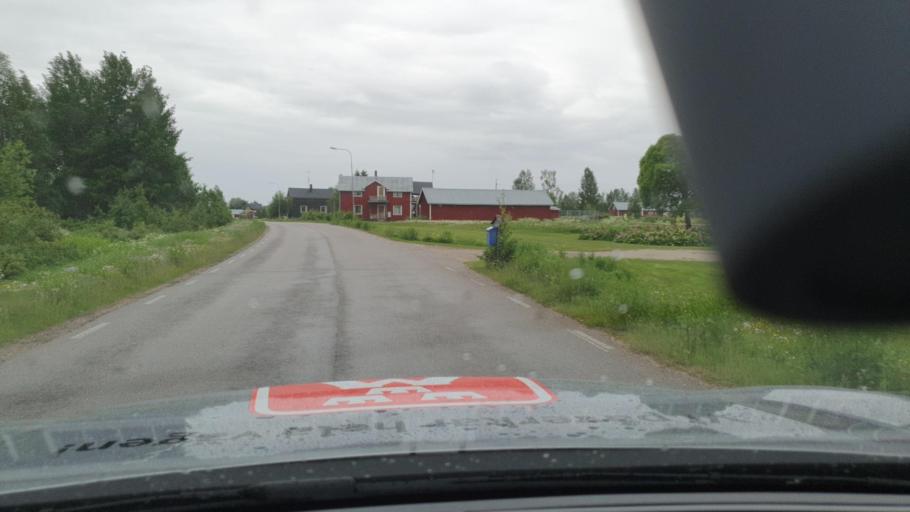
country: SE
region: Norrbotten
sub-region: Pajala Kommun
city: Pajala
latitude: 66.7986
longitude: 23.1233
